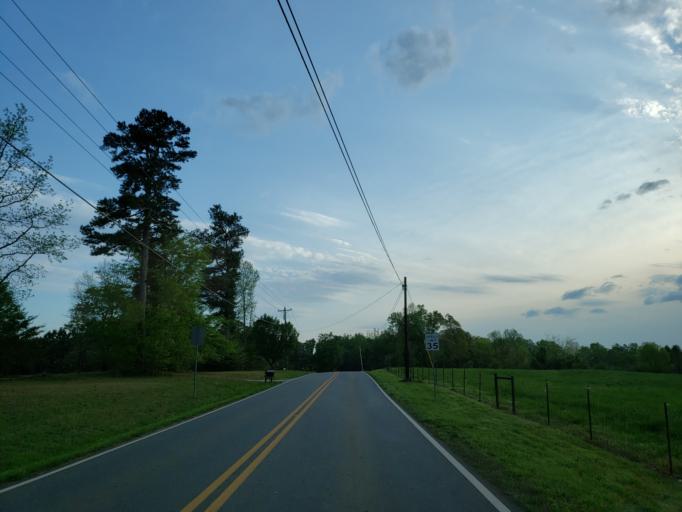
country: US
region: Georgia
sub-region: Cherokee County
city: Canton
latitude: 34.2932
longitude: -84.4517
